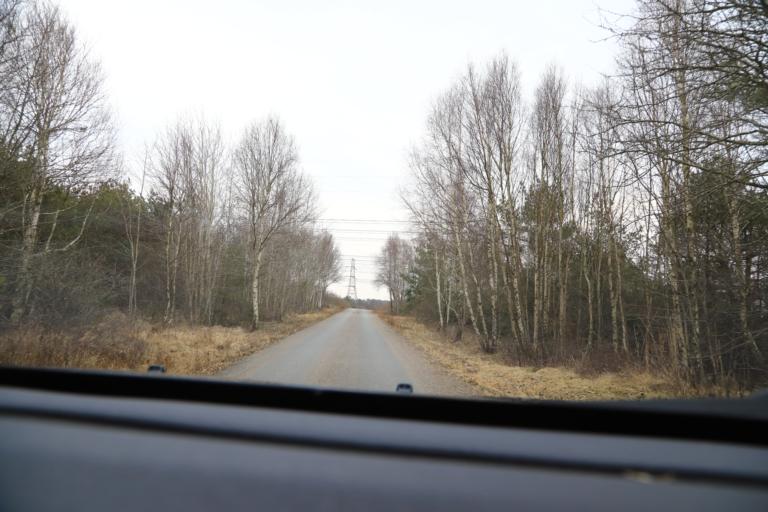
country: SE
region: Halland
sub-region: Kungsbacka Kommun
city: Frillesas
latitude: 57.2644
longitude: 12.1169
